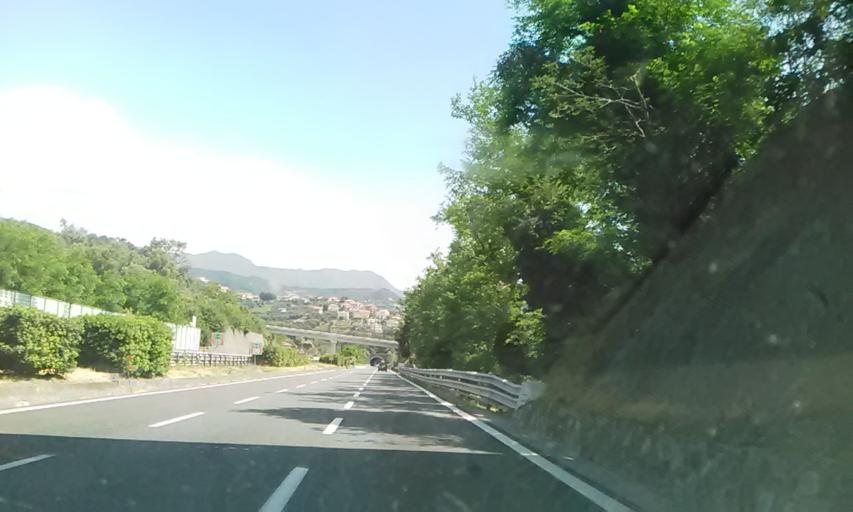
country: IT
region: Liguria
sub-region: Provincia di Savona
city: Celle Ligure
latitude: 44.3543
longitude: 8.5610
